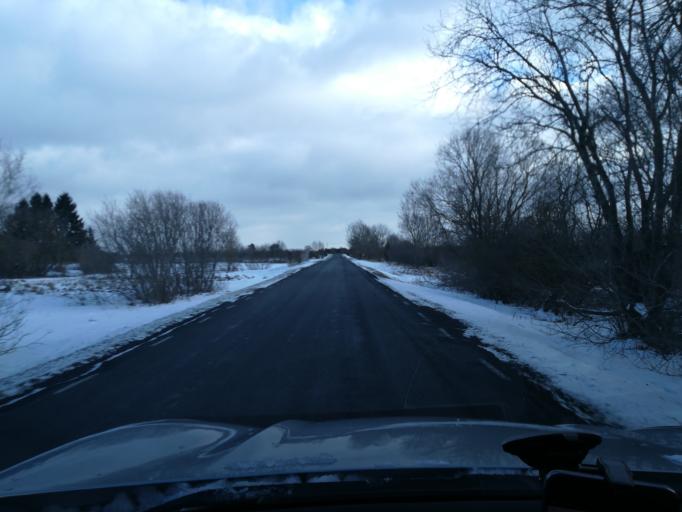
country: EE
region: Harju
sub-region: Keila linn
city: Keila
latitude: 59.4350
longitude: 24.4010
